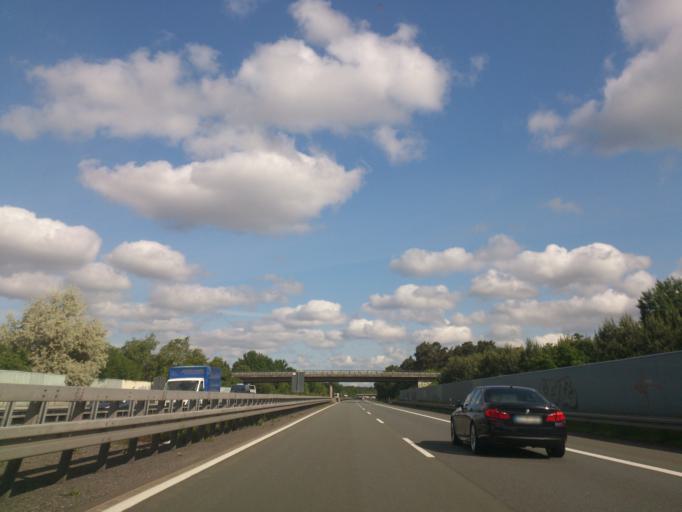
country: DE
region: North Rhine-Westphalia
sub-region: Regierungsbezirk Detmold
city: Hovelhof
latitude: 51.8694
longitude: 8.6557
